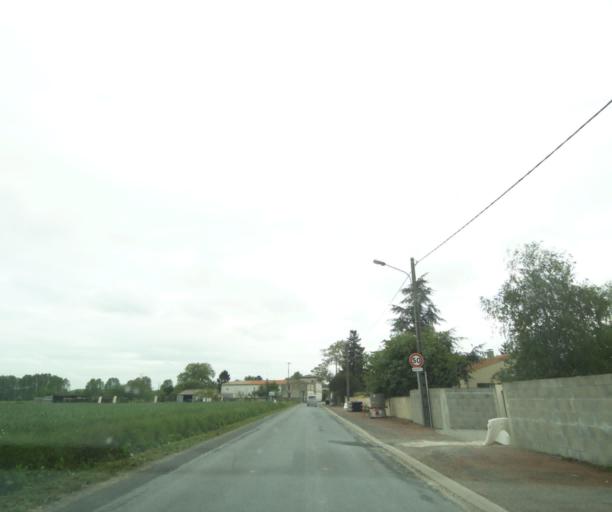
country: FR
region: Poitou-Charentes
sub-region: Departement de la Charente-Maritime
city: Chaniers
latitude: 45.6991
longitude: -0.5282
